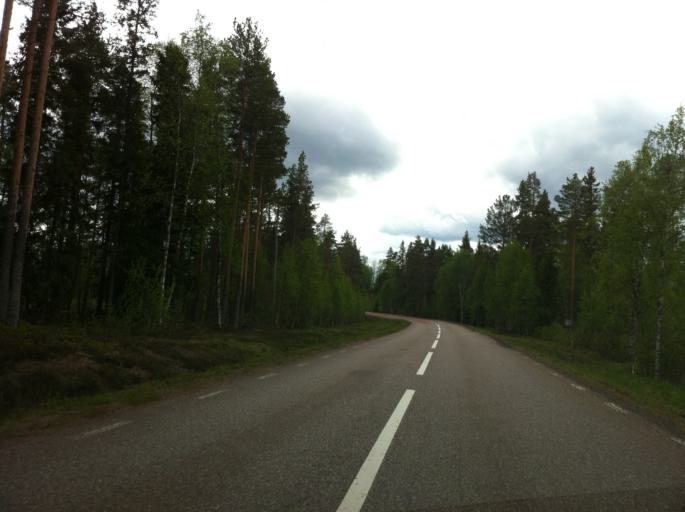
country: NO
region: Hedmark
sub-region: Trysil
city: Innbygda
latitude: 61.4354
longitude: 13.0979
